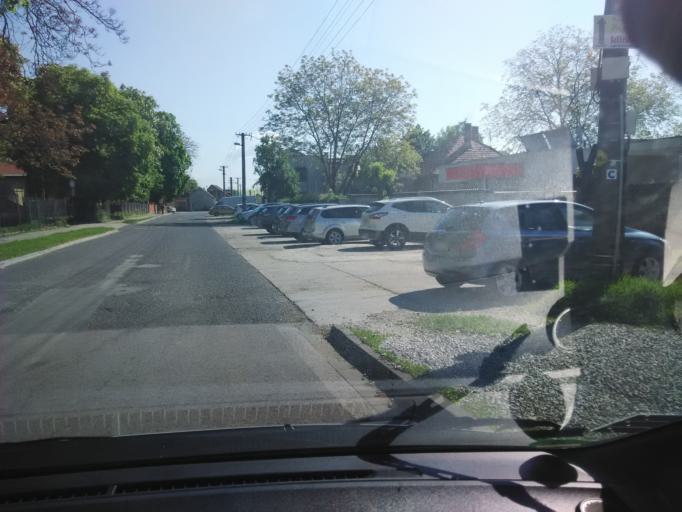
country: SK
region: Nitriansky
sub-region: Okres Nitra
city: Nitra
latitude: 48.2731
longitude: 18.0994
